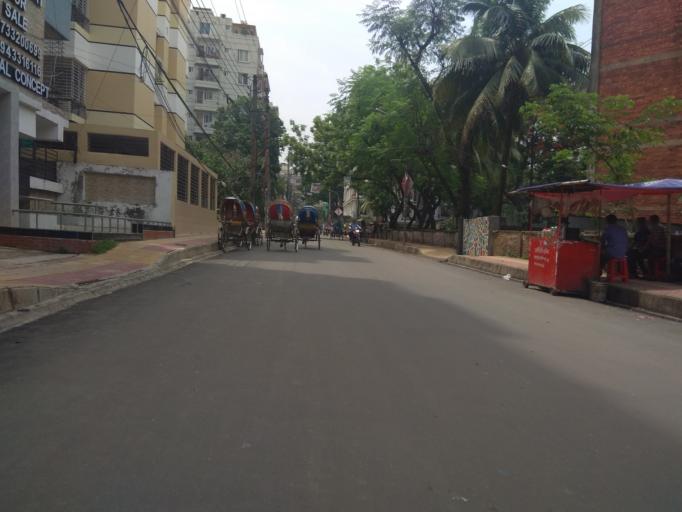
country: BD
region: Dhaka
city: Azimpur
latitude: 23.8063
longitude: 90.3561
